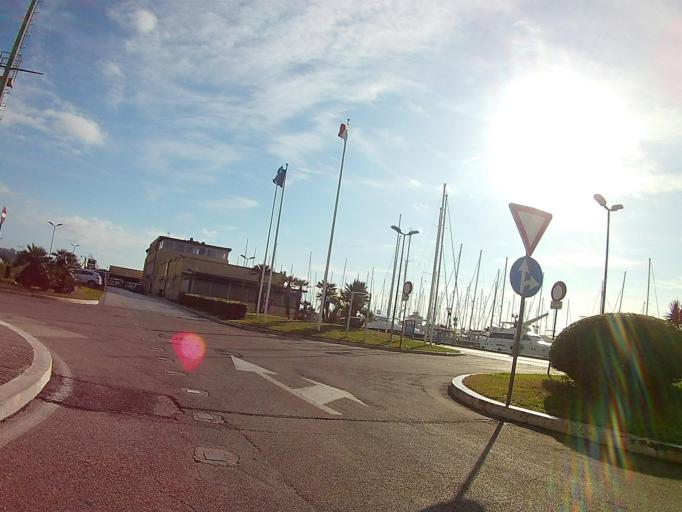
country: IT
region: Latium
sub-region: Citta metropolitana di Roma Capitale
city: Fiumicino-Isola Sacra
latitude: 41.7401
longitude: 12.2418
